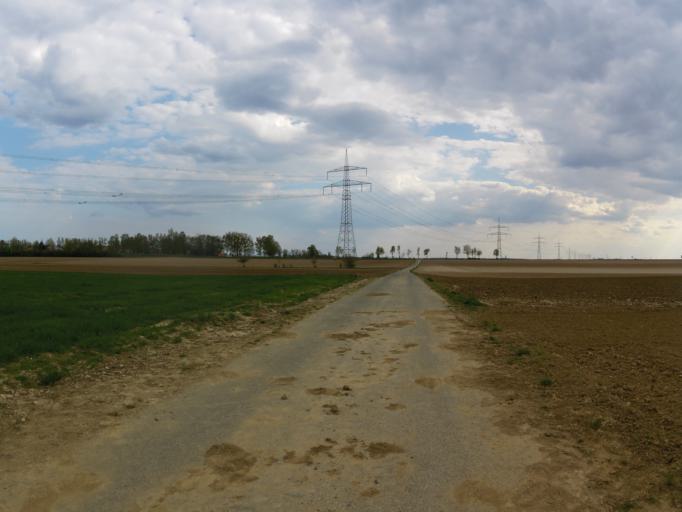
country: DE
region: Bavaria
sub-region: Regierungsbezirk Unterfranken
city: Oberpleichfeld
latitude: 49.8575
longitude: 10.0955
